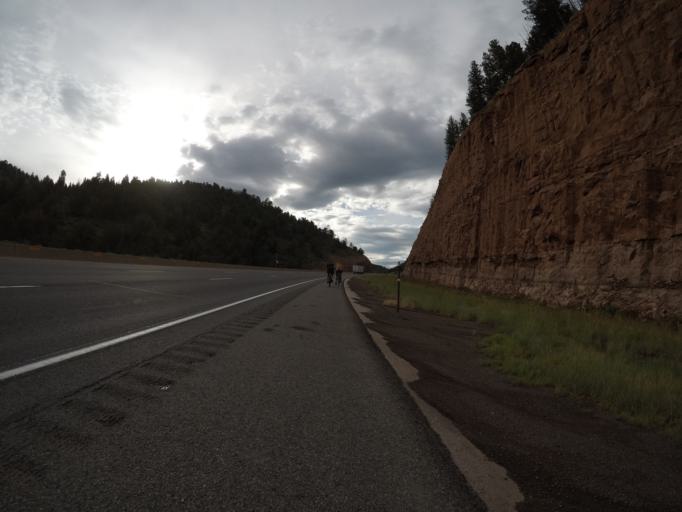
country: US
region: Wyoming
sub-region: Albany County
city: Laramie
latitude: 41.2651
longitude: -105.4681
